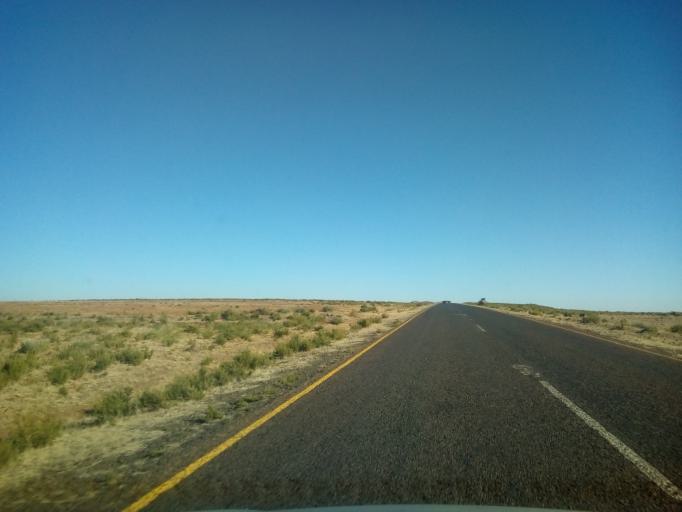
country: LS
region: Berea
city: Teyateyaneng
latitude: -29.2559
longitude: 27.7464
